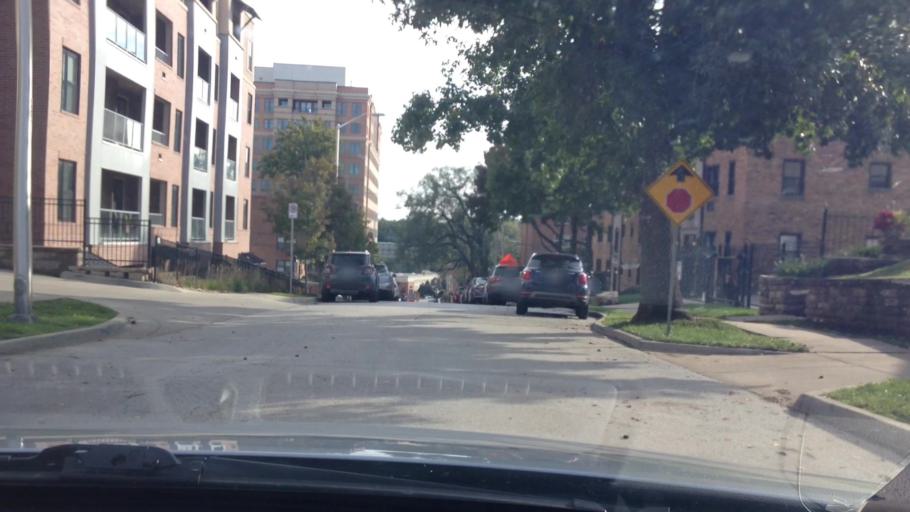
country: US
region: Kansas
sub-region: Johnson County
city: Westwood
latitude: 39.0451
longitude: -94.5933
